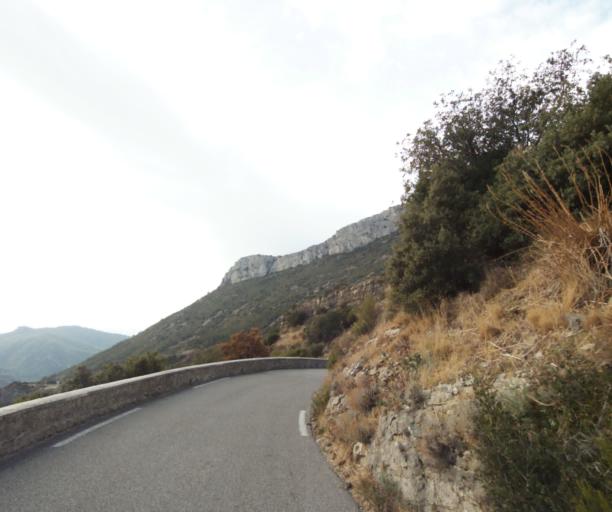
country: FR
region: Provence-Alpes-Cote d'Azur
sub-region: Departement des Bouches-du-Rhone
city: Gemenos
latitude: 43.3125
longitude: 5.6671
